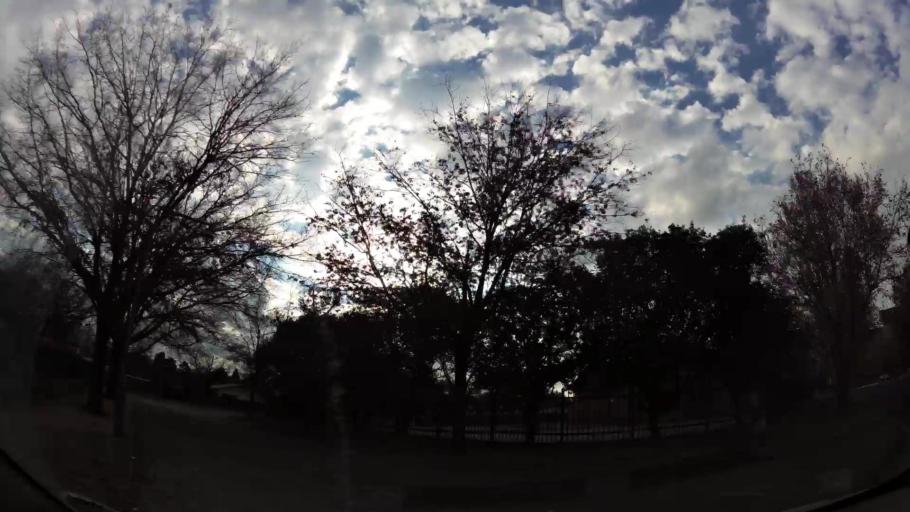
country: ZA
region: Orange Free State
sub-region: Fezile Dabi District Municipality
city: Sasolburg
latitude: -26.8210
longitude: 27.8241
